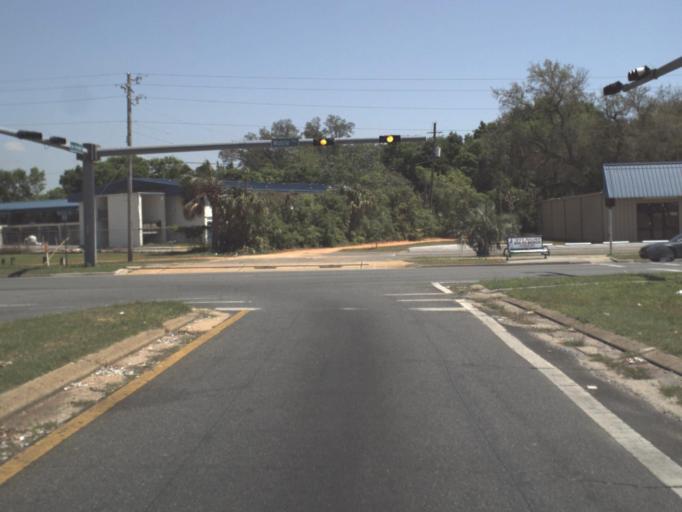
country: US
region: Florida
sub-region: Escambia County
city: West Pensacola
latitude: 30.4277
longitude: -87.2698
